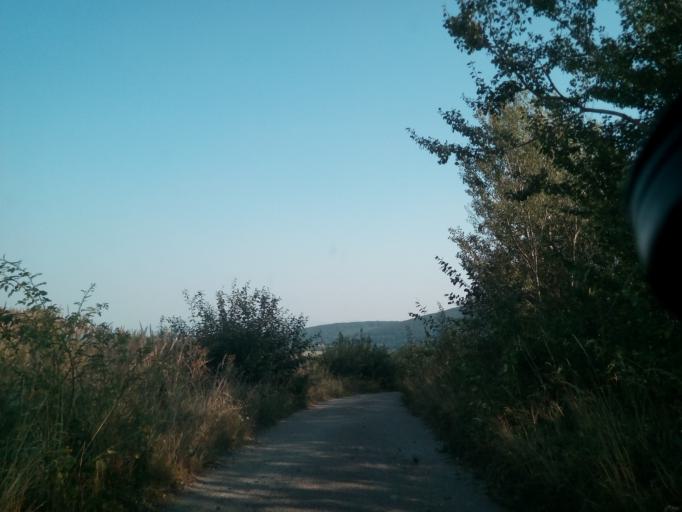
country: SK
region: Kosicky
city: Moldava nad Bodvou
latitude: 48.7323
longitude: 21.0995
